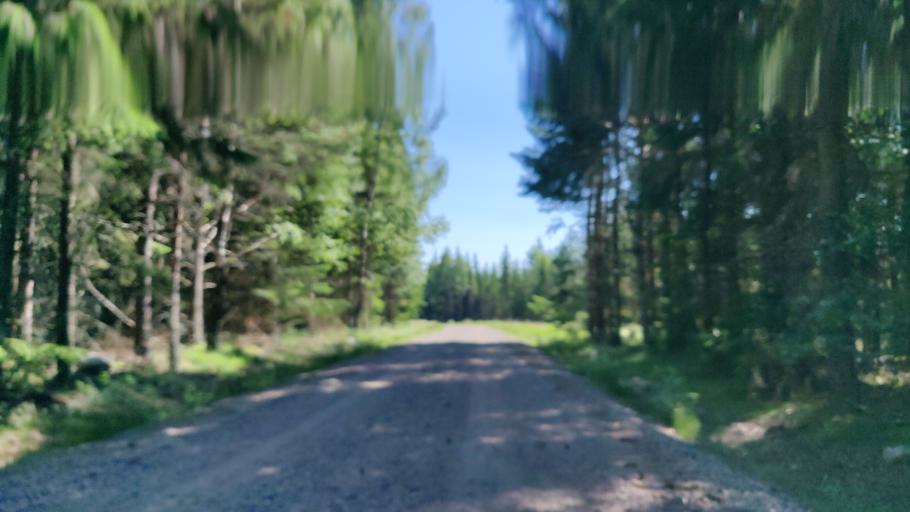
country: SE
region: Vaermland
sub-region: Hagfors Kommun
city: Hagfors
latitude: 59.9806
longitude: 13.5978
